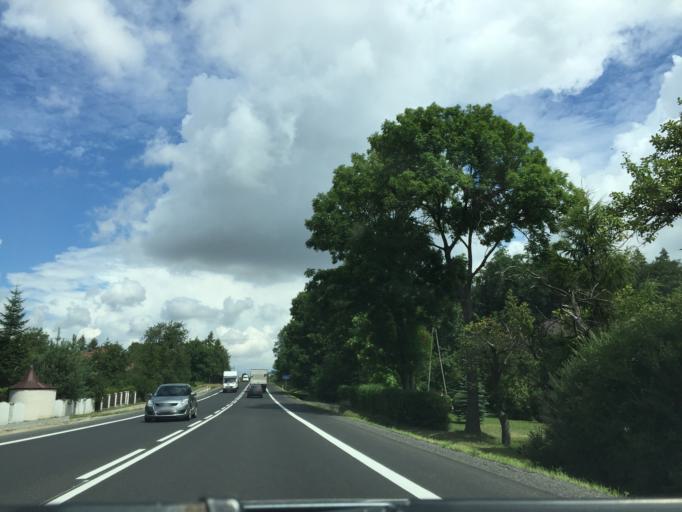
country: PL
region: Lesser Poland Voivodeship
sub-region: Powiat krakowski
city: Michalowice
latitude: 50.1961
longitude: 20.0073
